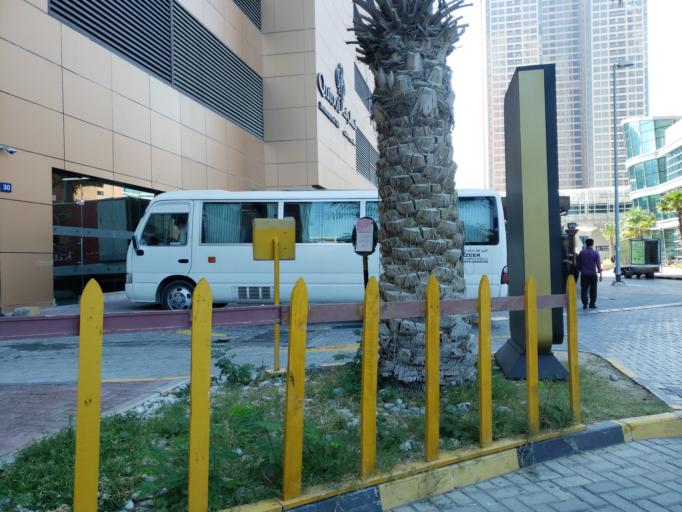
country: AE
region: Dubai
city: Dubai
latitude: 25.1030
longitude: 55.1718
